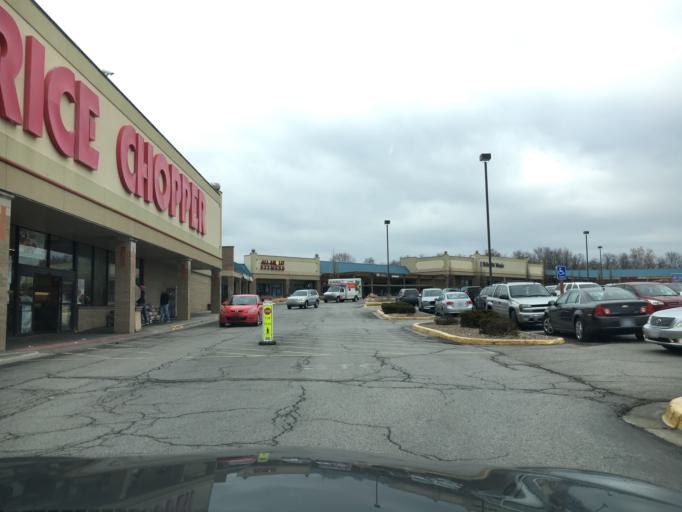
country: US
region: Kansas
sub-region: Johnson County
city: Overland Park
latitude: 38.9142
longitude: -94.6724
